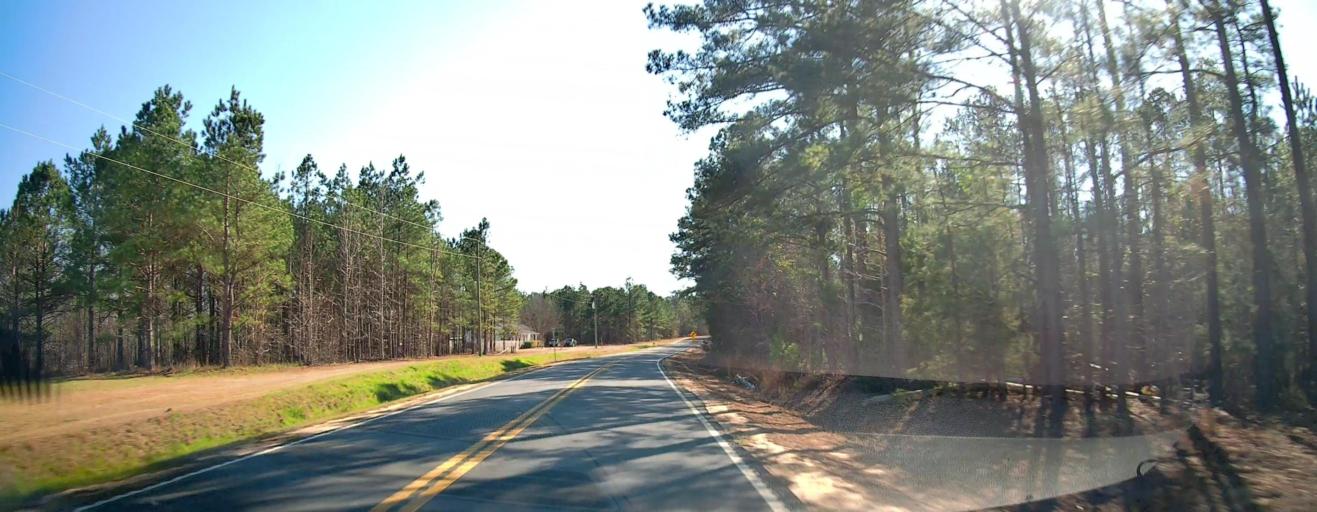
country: US
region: Georgia
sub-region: Taylor County
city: Butler
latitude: 32.6577
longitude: -84.3640
